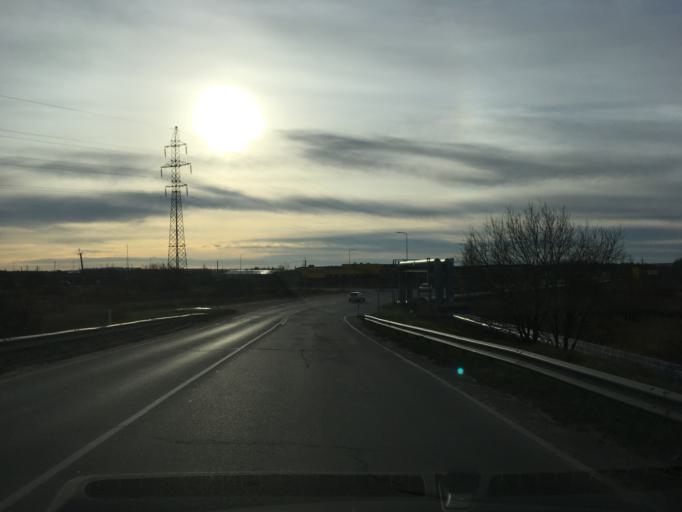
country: EE
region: Ida-Virumaa
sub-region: Narva linn
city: Narva
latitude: 59.3705
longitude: 28.1553
